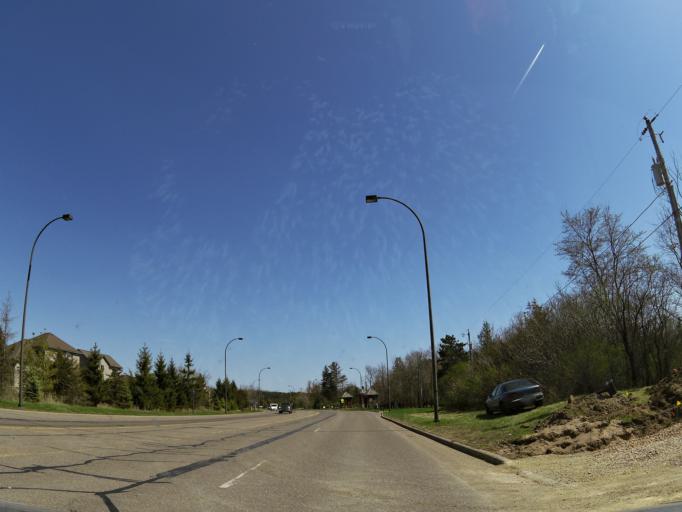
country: US
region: Wisconsin
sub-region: Saint Croix County
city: Hudson
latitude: 44.9599
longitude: -92.7034
